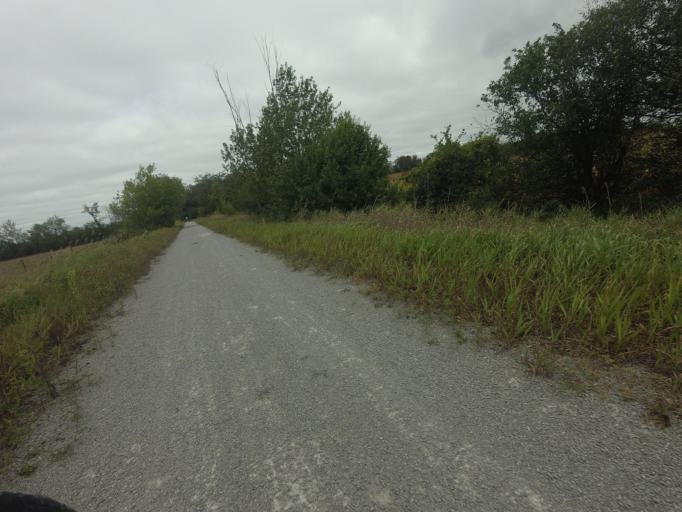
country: CA
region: Ontario
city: Uxbridge
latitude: 44.3074
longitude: -78.8944
